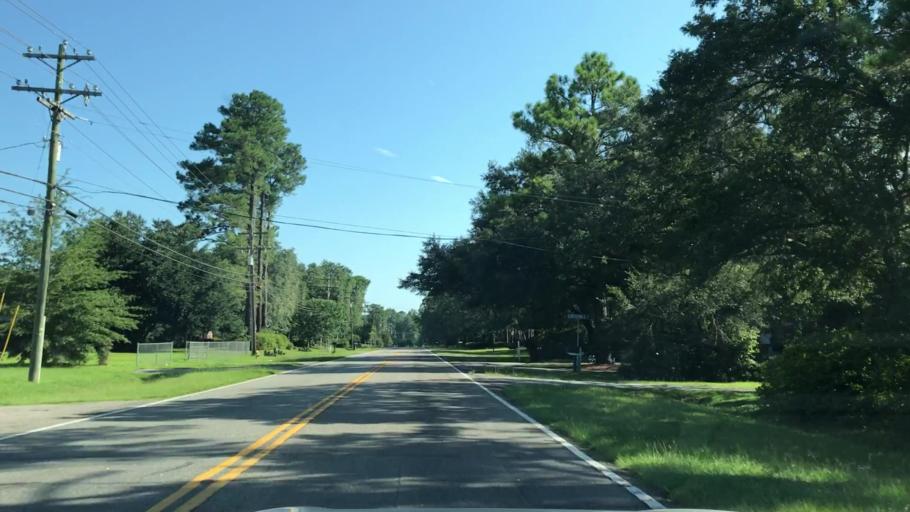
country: US
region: South Carolina
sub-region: Georgetown County
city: Georgetown
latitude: 33.4323
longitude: -79.2780
